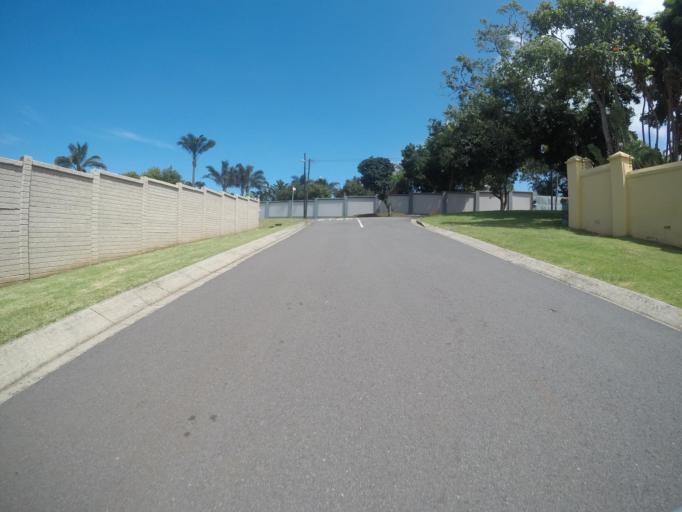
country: ZA
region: Eastern Cape
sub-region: Buffalo City Metropolitan Municipality
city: East London
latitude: -32.9743
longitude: 27.9085
